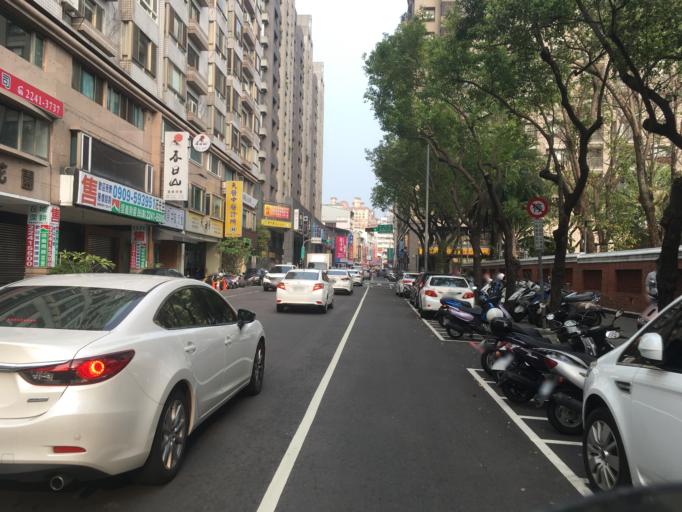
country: TW
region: Taiwan
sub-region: Taichung City
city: Taichung
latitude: 24.1757
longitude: 120.6875
